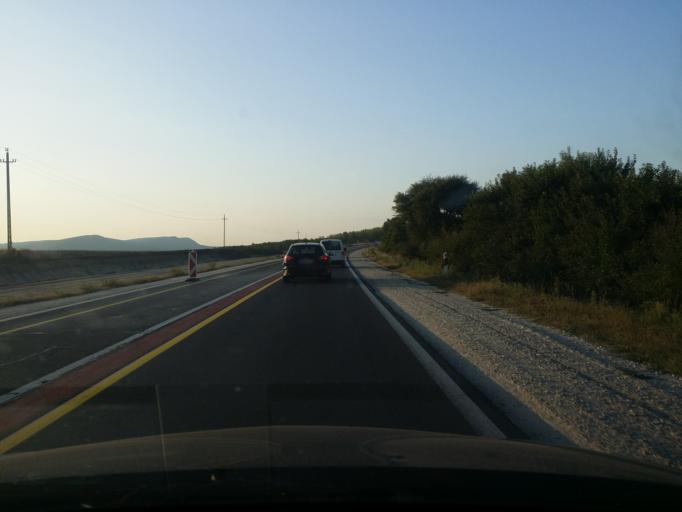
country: HU
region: Pest
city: Dunakeszi
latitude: 47.6460
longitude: 19.1622
